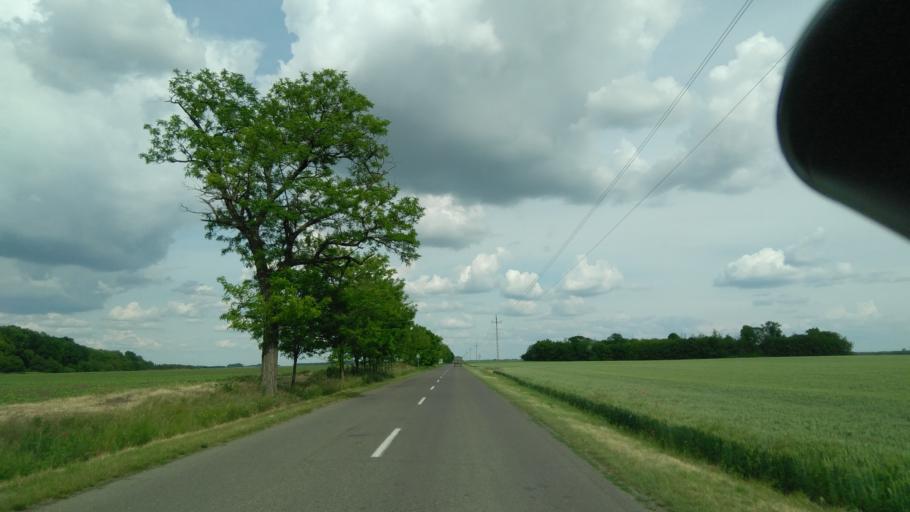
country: HU
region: Bekes
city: Mezohegyes
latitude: 46.3146
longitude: 20.8379
